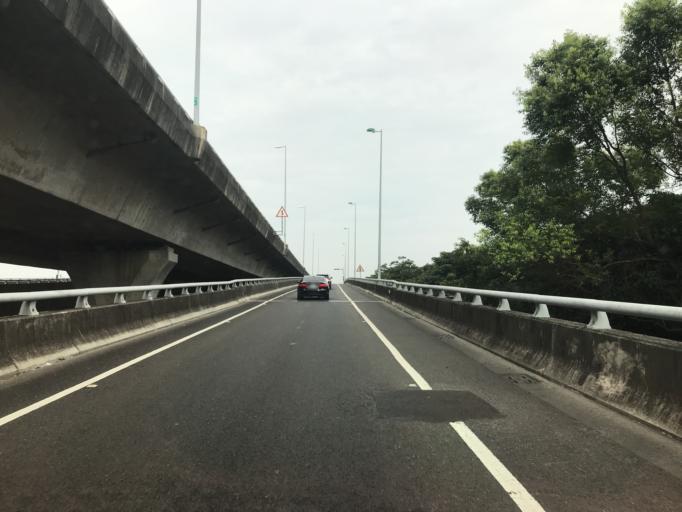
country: TW
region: Taiwan
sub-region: Pingtung
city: Pingtung
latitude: 22.6462
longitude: 120.5425
